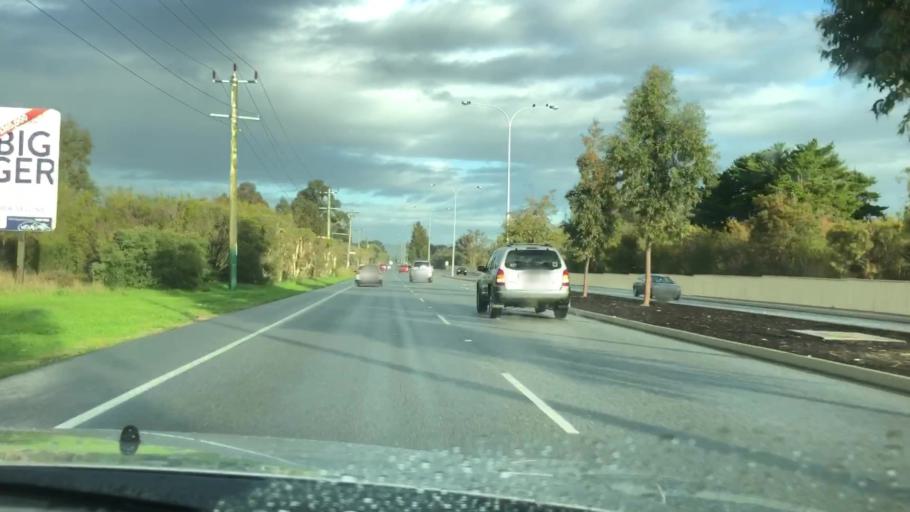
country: AU
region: Western Australia
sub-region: Armadale
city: Harrisdale
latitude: -32.1097
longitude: 115.9414
